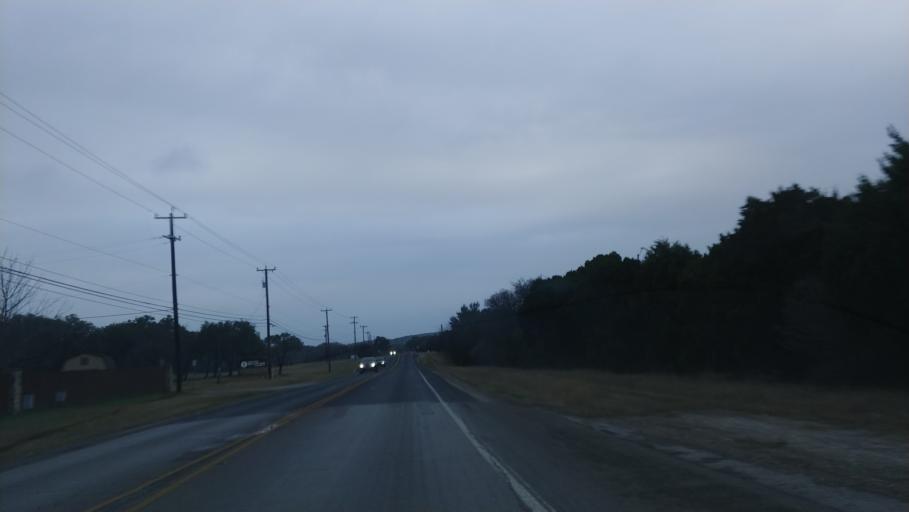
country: US
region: Texas
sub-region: Bexar County
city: Cross Mountain
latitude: 29.6714
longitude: -98.6525
